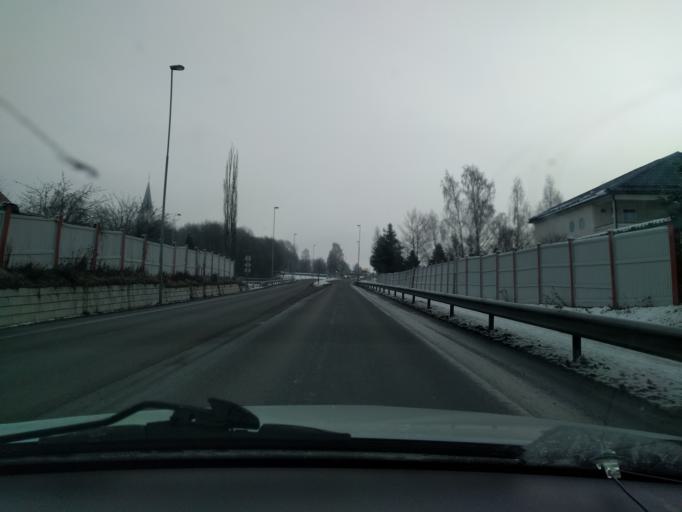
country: NO
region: Hedmark
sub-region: Hamar
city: Hamar
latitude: 60.8011
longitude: 11.1268
